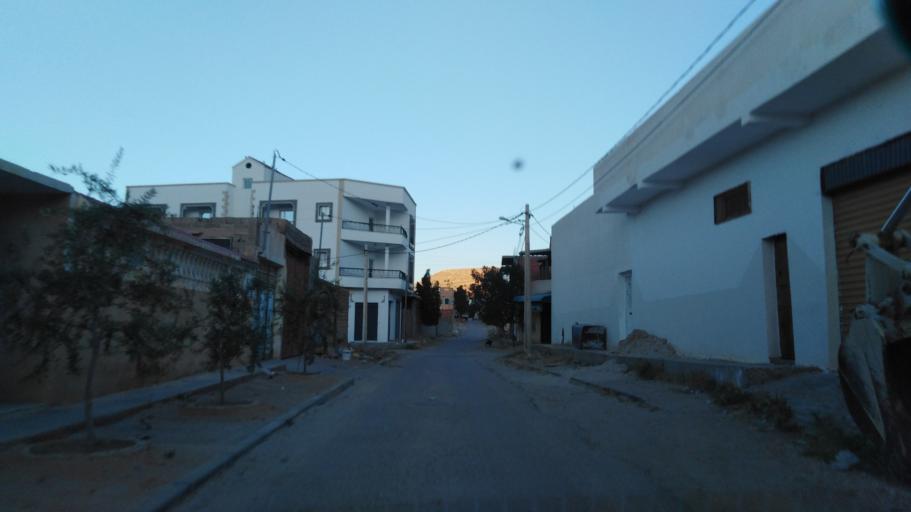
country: TN
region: Tataouine
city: Tataouine
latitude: 32.9420
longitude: 10.4540
